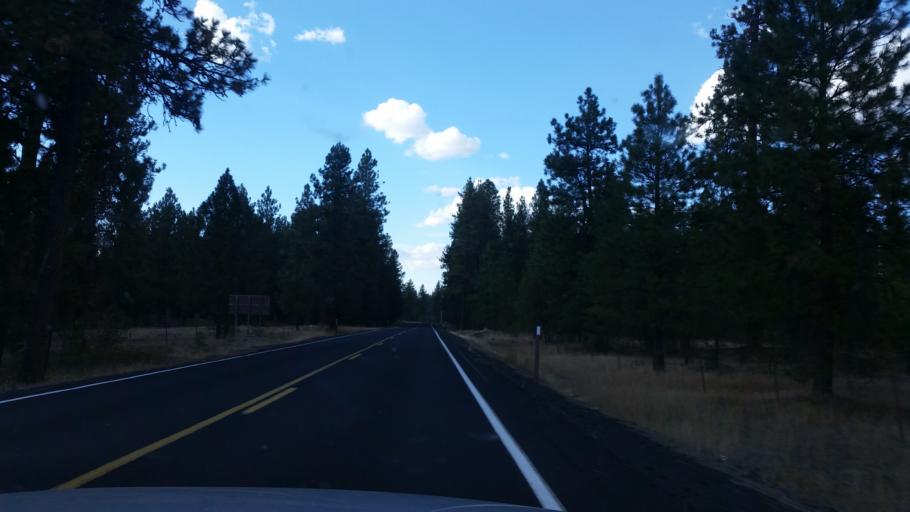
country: US
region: Washington
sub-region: Spokane County
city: Cheney
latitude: 47.4550
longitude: -117.5777
